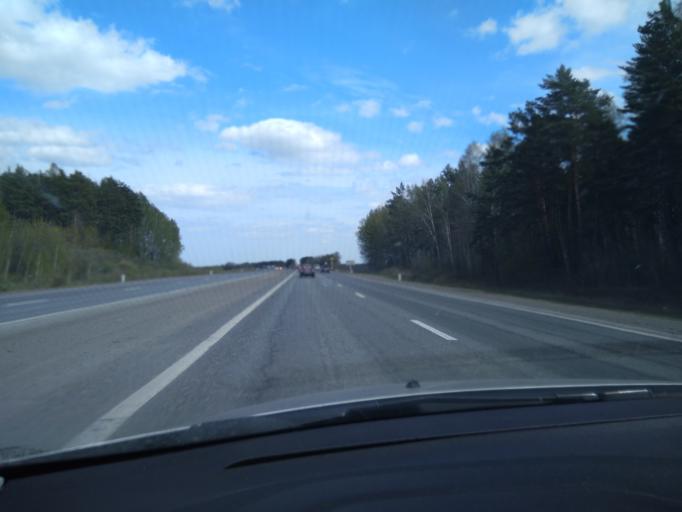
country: RU
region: Tjumen
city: Moskovskiy
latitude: 57.0981
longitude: 65.2829
